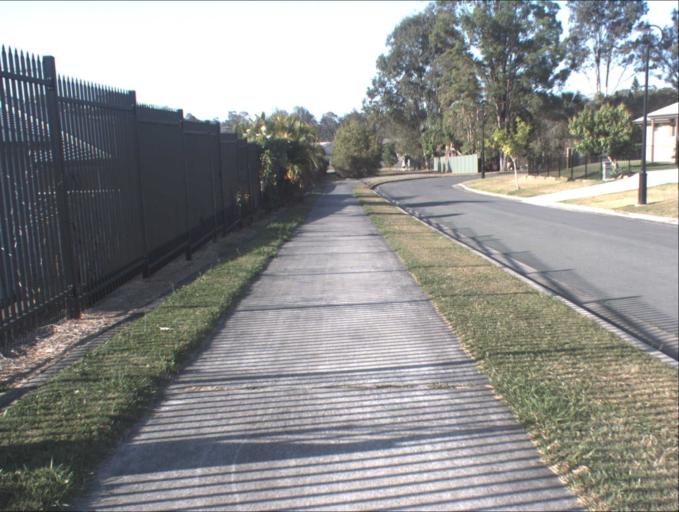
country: AU
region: Queensland
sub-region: Gold Coast
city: Yatala
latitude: -27.7087
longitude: 153.2202
